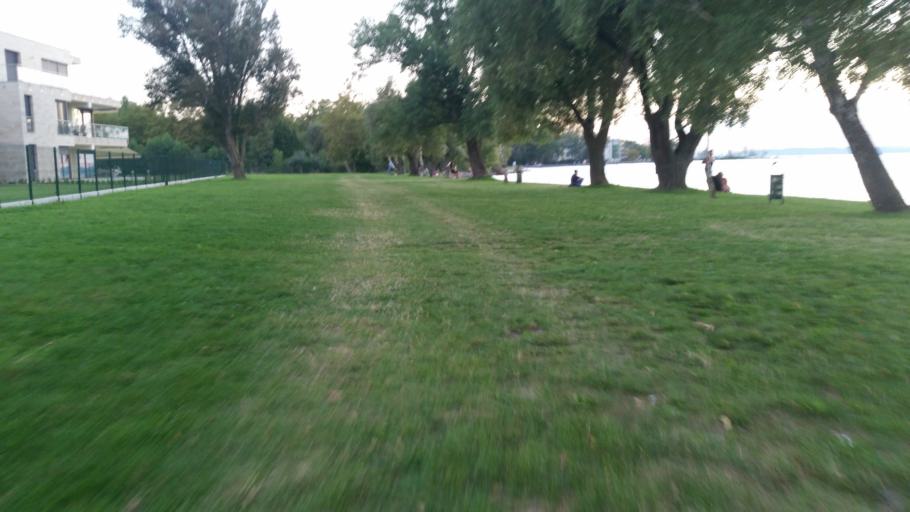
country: HU
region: Somogy
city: Siofok
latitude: 46.9039
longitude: 18.0242
